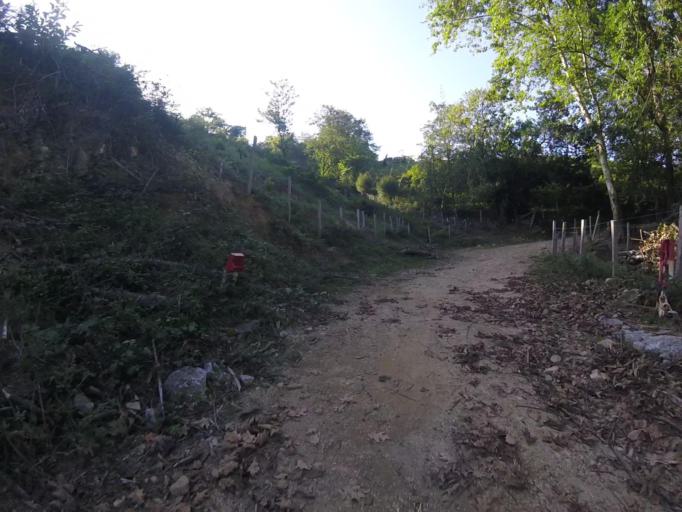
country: ES
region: Basque Country
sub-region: Provincia de Guipuzcoa
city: Irun
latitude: 43.3118
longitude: -1.7498
